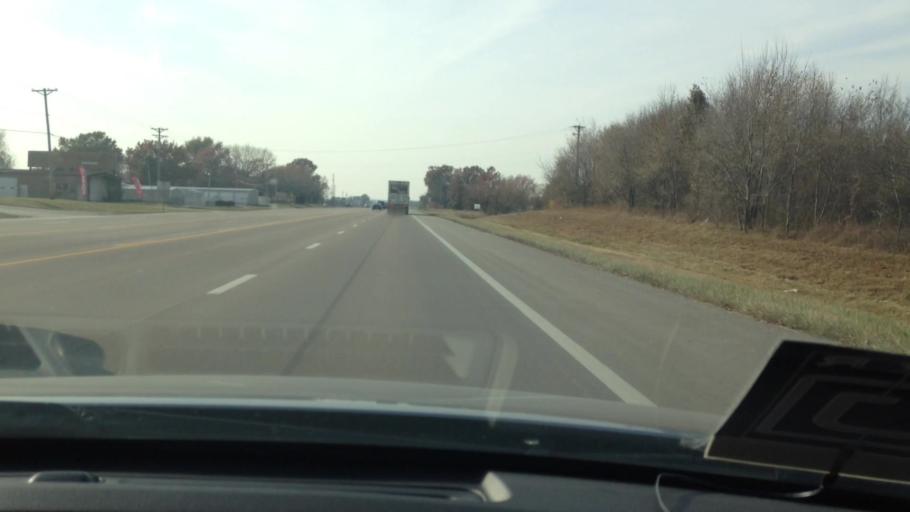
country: US
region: Missouri
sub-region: Henry County
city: Clinton
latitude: 38.3895
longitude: -93.8006
